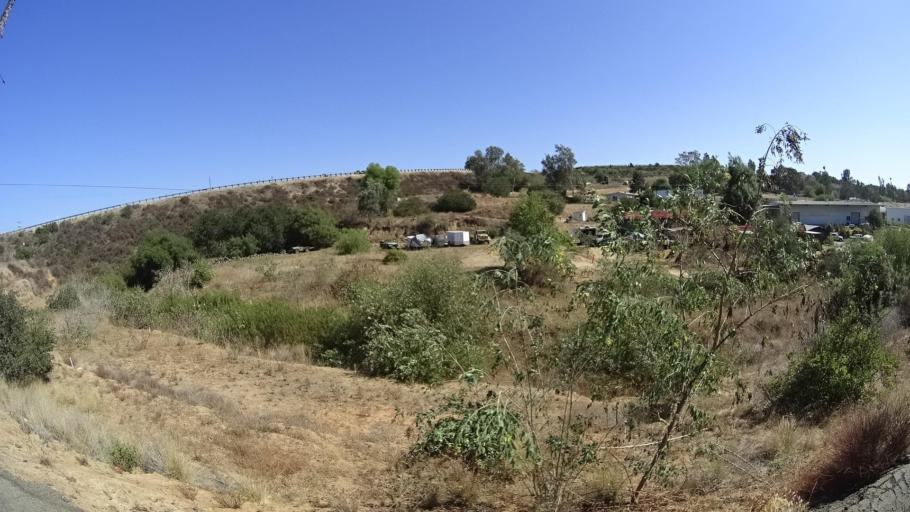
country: US
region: California
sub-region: San Diego County
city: Bonsall
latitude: 33.3011
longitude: -117.1551
